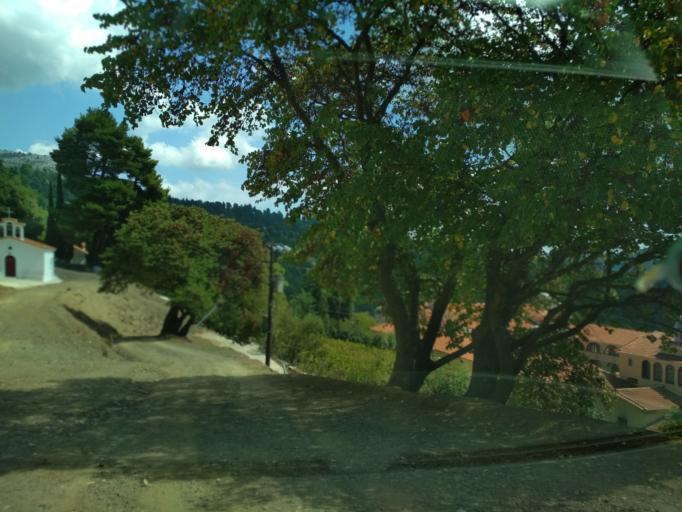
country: GR
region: Central Greece
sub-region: Nomos Evvoias
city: Roviai
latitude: 38.8461
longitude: 23.2810
